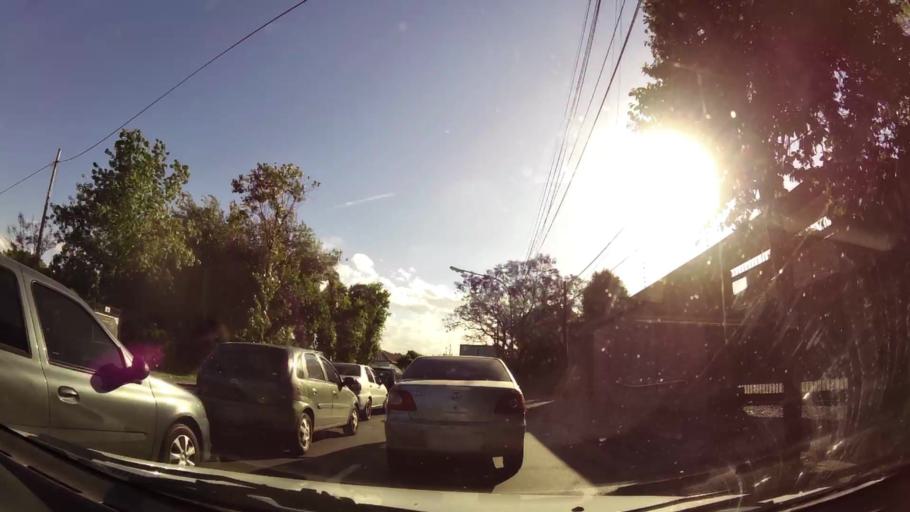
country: AR
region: Buenos Aires
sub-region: Partido de San Isidro
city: San Isidro
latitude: -34.4904
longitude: -58.5438
